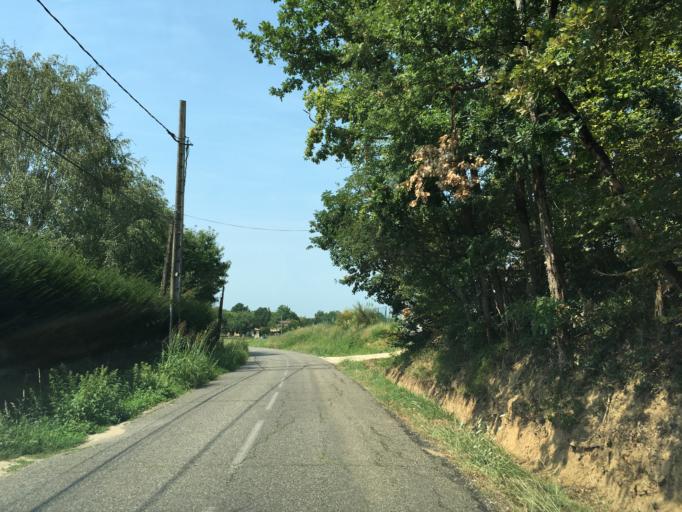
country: FR
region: Midi-Pyrenees
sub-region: Departement du Tarn-et-Garonne
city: Saint-Nauphary
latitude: 43.9898
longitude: 1.4159
